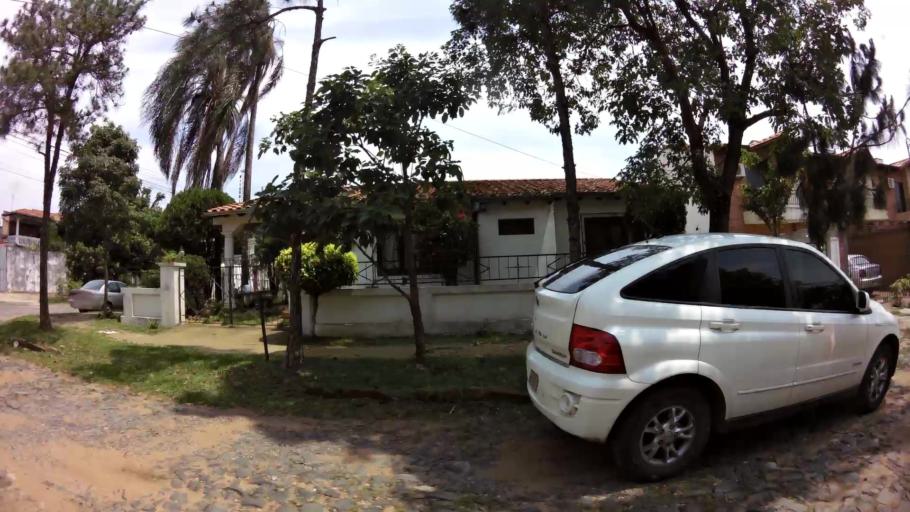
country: PY
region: Central
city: Fernando de la Mora
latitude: -25.3183
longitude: -57.5620
